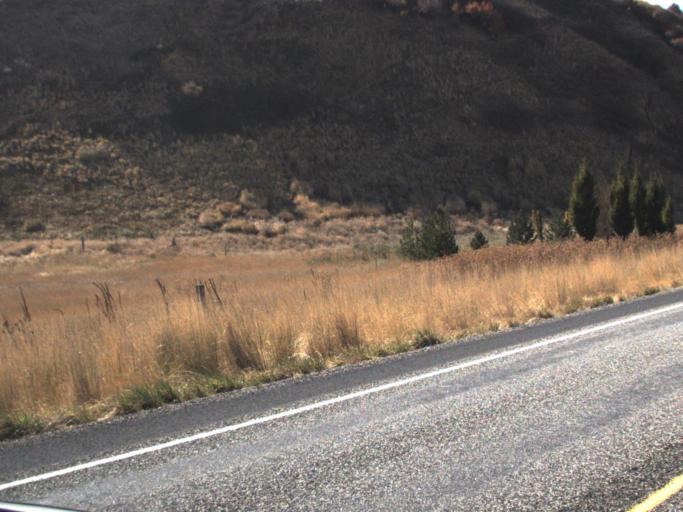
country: US
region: Washington
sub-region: Walla Walla County
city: Waitsburg
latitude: 46.2688
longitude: -118.1789
